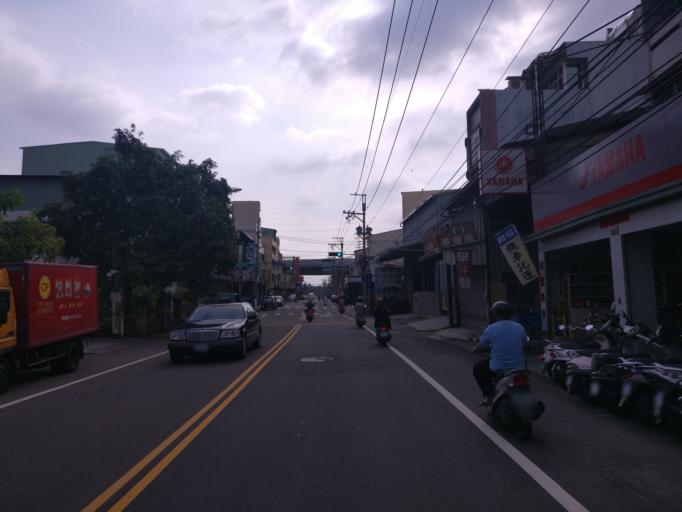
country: TW
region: Taiwan
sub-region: Taichung City
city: Taichung
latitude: 24.0661
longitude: 120.6925
